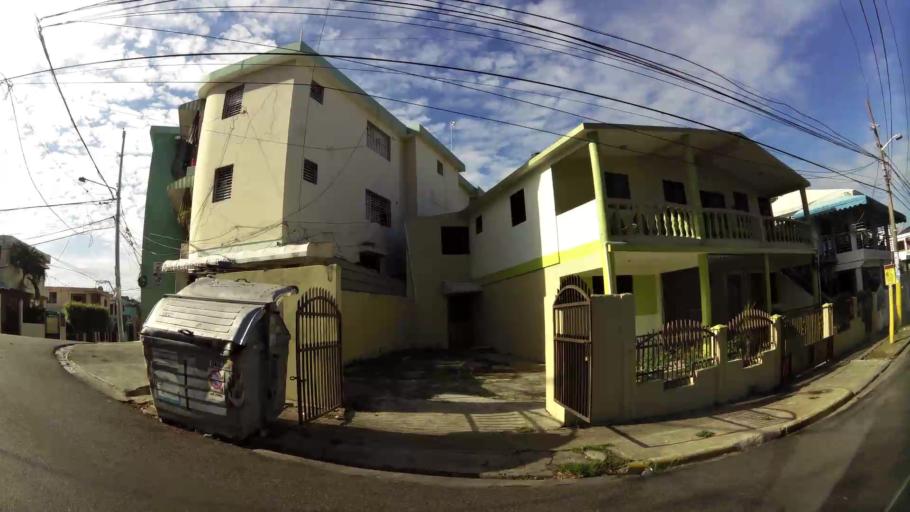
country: DO
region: Santo Domingo
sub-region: Santo Domingo
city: Santo Domingo Este
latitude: 18.4869
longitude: -69.8598
